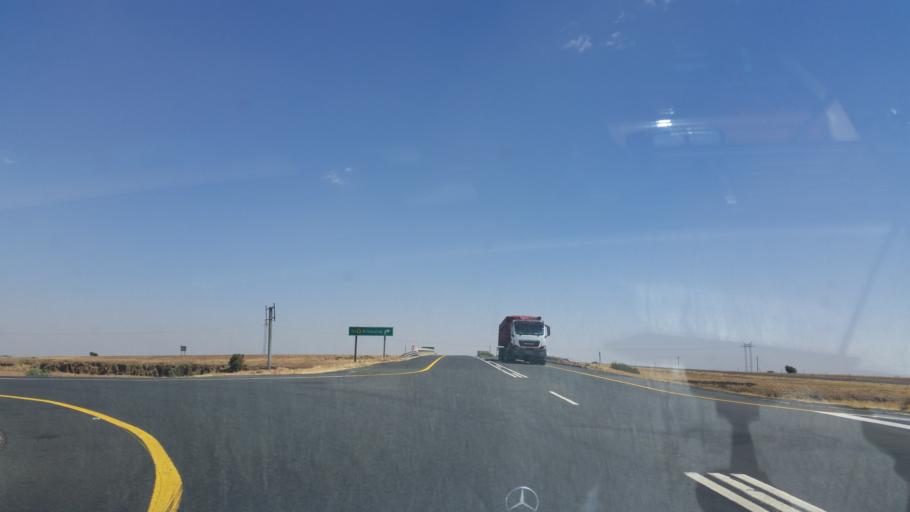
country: ZA
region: Orange Free State
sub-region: Lejweleputswa District Municipality
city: Winburg
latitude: -28.4990
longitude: 26.9982
